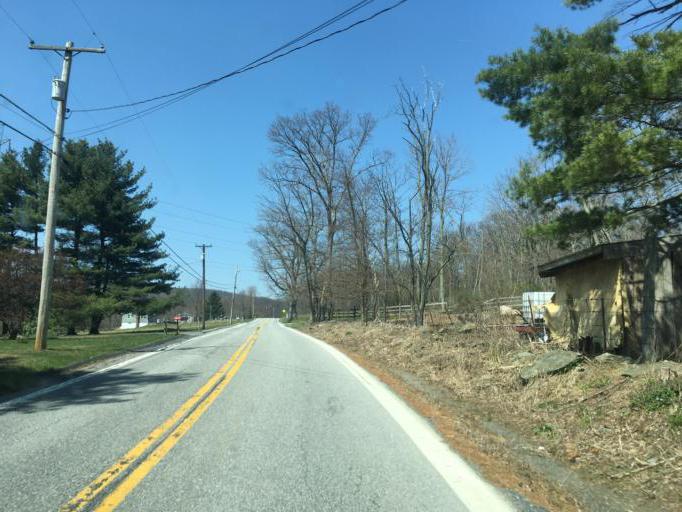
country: US
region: Maryland
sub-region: Washington County
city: Cavetown
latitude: 39.6110
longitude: -77.5563
